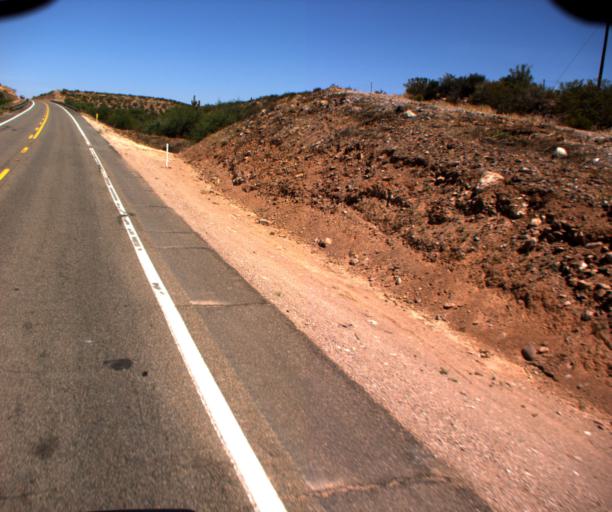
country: US
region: Arizona
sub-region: Graham County
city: Bylas
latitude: 33.2161
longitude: -110.2137
